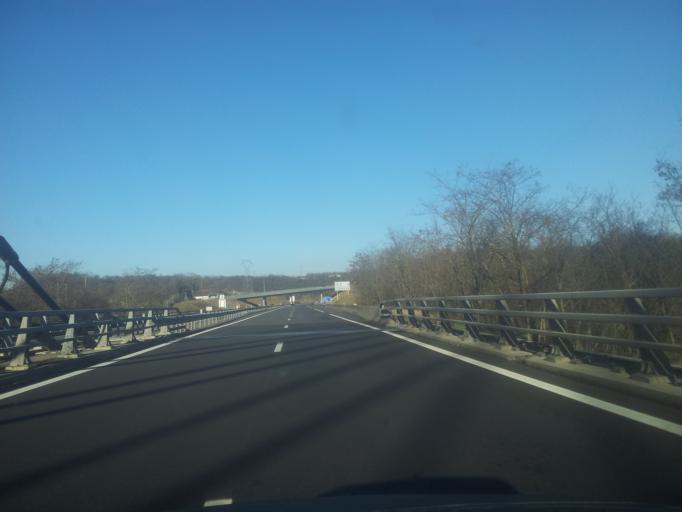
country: FR
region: Rhone-Alpes
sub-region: Departement de l'Isere
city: Saint-Lattier
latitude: 45.0838
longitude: 5.2156
